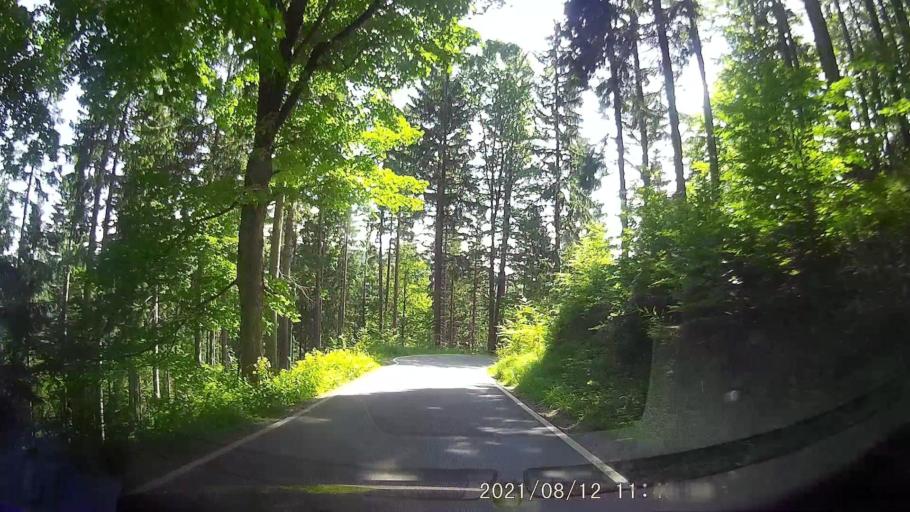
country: PL
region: Lower Silesian Voivodeship
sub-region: Powiat klodzki
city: Stronie Slaskie
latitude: 50.2504
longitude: 16.8437
